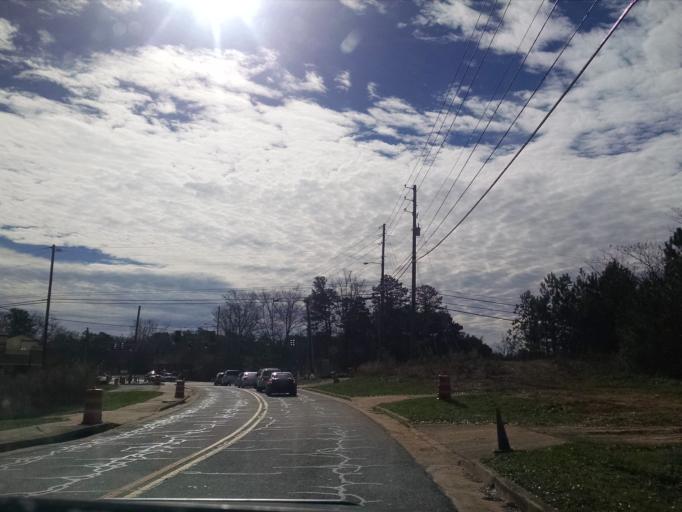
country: US
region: Georgia
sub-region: Gwinnett County
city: Sugar Hill
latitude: 34.1122
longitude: -84.0405
